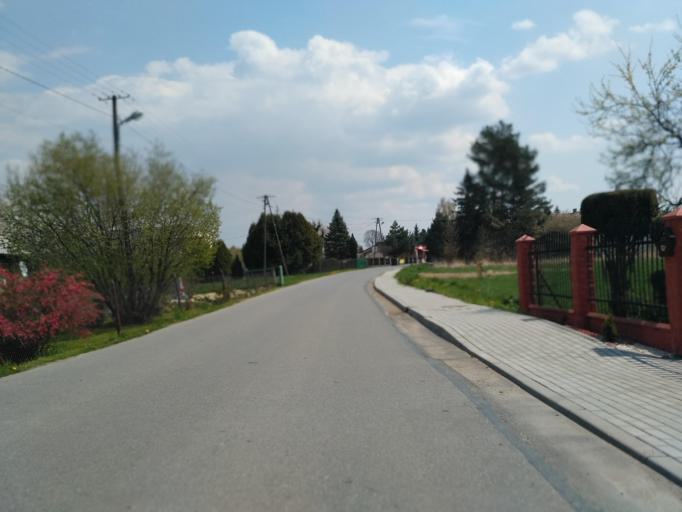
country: PL
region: Subcarpathian Voivodeship
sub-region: Powiat jasielski
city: Tarnowiec
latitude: 49.7397
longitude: 21.5346
